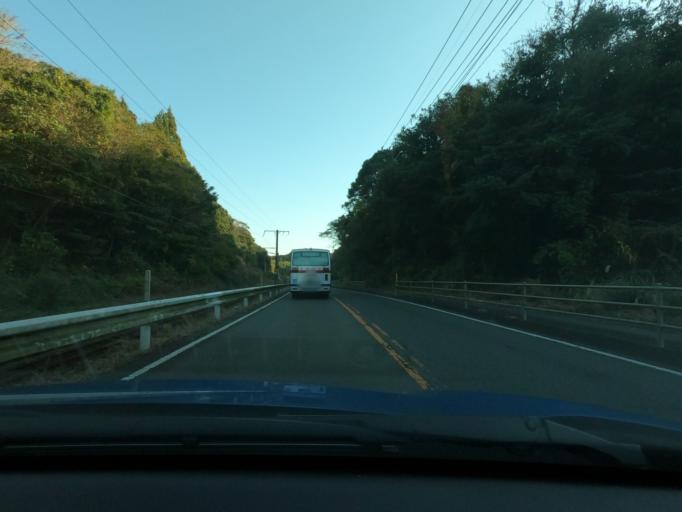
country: JP
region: Kagoshima
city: Akune
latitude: 31.9969
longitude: 130.1966
